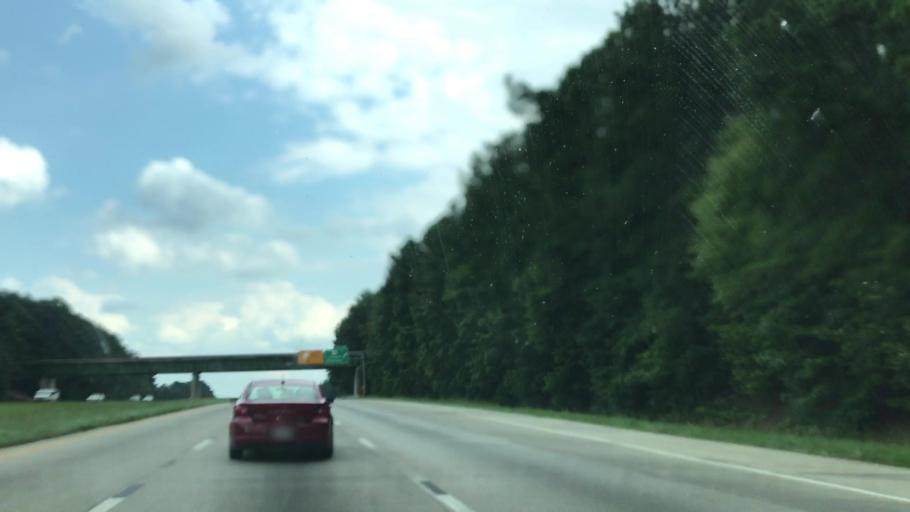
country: US
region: South Carolina
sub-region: Fairfield County
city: Winnsboro Mills
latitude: 34.3144
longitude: -81.0035
